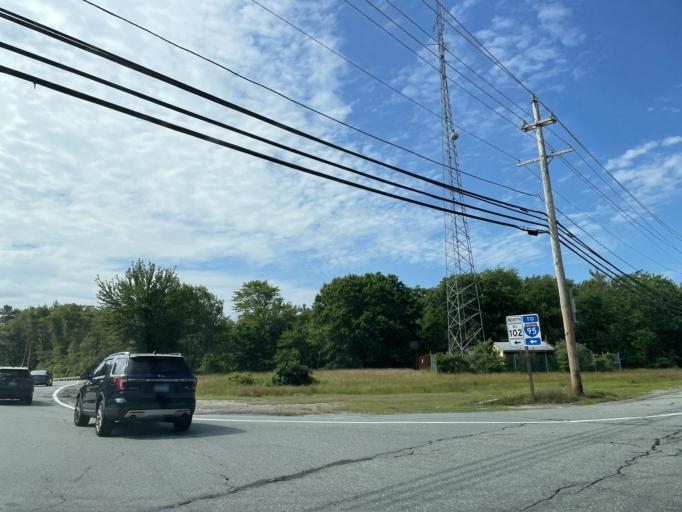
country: US
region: Rhode Island
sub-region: Kent County
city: West Greenwich
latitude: 41.5956
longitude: -71.6472
